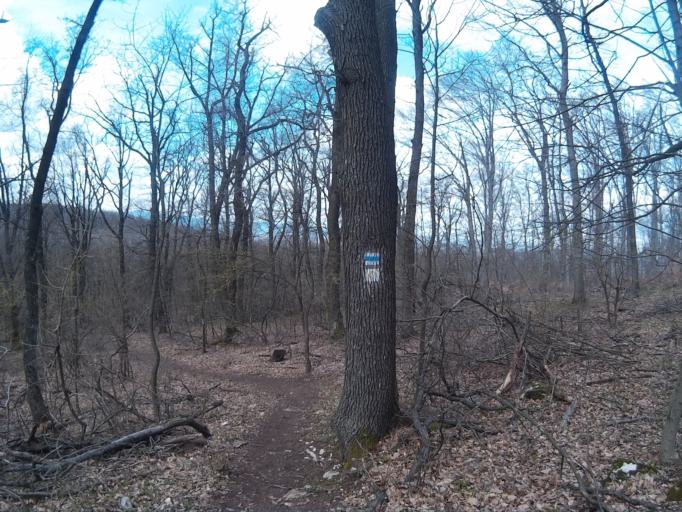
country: HU
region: Pest
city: Kosd
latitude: 47.8342
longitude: 19.1462
